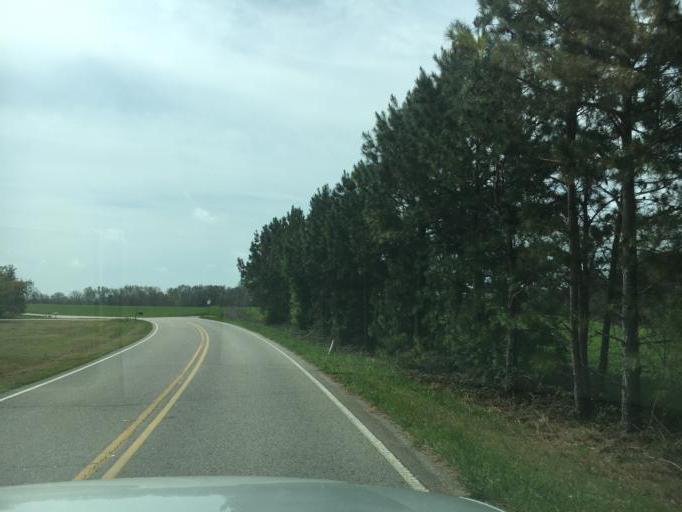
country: US
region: Georgia
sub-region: Hart County
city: Royston
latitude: 34.3085
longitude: -83.0487
